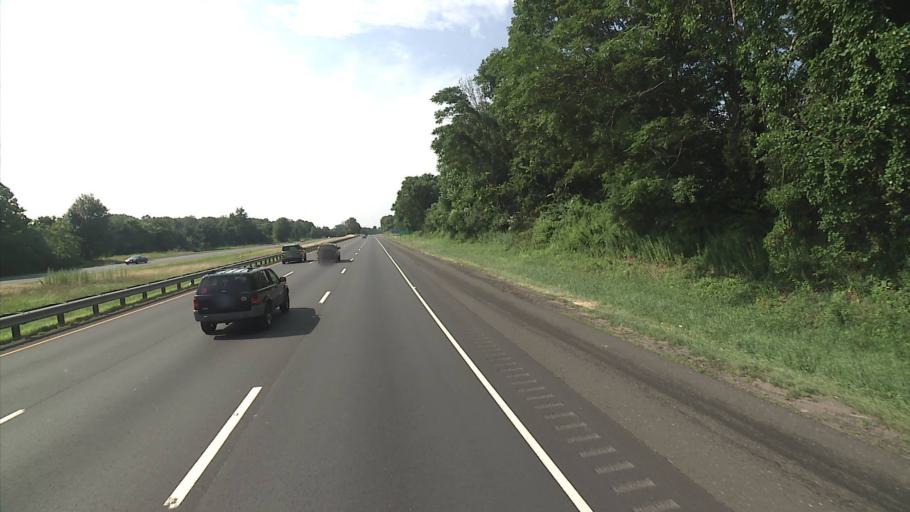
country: US
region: Connecticut
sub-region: New Haven County
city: Meriden
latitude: 41.4961
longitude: -72.7684
